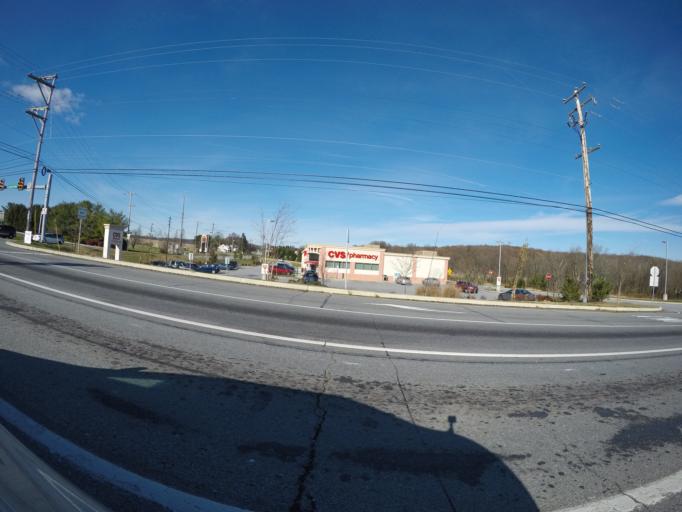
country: US
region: Pennsylvania
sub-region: Chester County
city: Parkesburg
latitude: 39.9834
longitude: -75.9319
